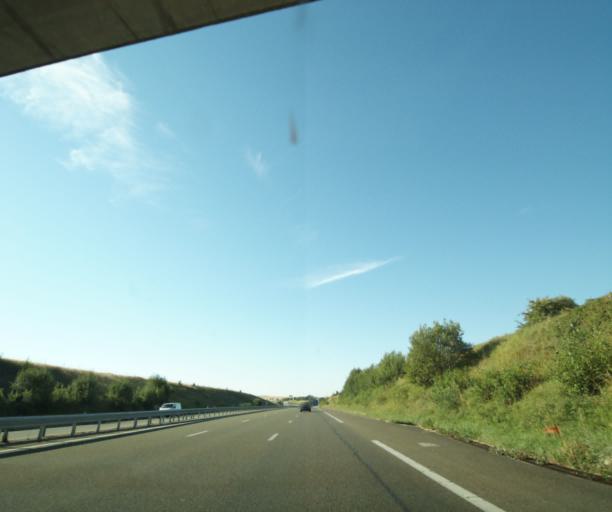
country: FR
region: Bourgogne
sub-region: Departement de l'Yonne
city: Sergines
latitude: 48.2868
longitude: 3.2682
